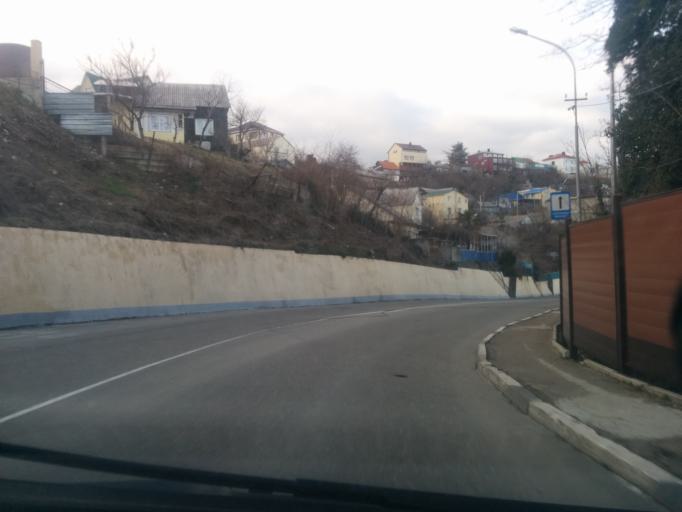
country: RU
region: Krasnodarskiy
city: Tuapse
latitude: 44.1021
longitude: 39.0662
